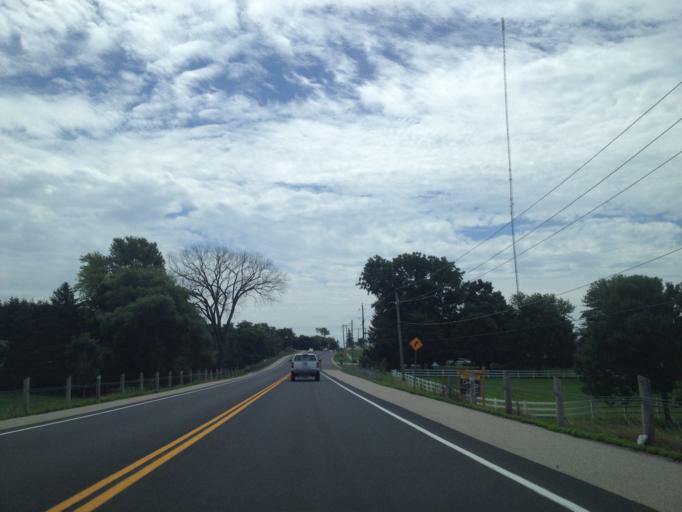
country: CA
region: Ontario
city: Ingersoll
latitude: 43.0157
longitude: -80.8388
